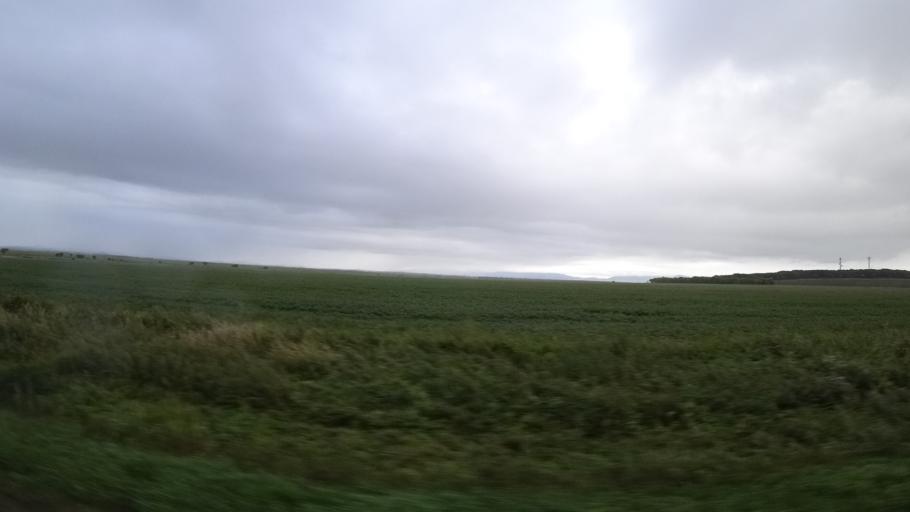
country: RU
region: Primorskiy
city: Chernigovka
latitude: 44.3761
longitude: 132.5297
